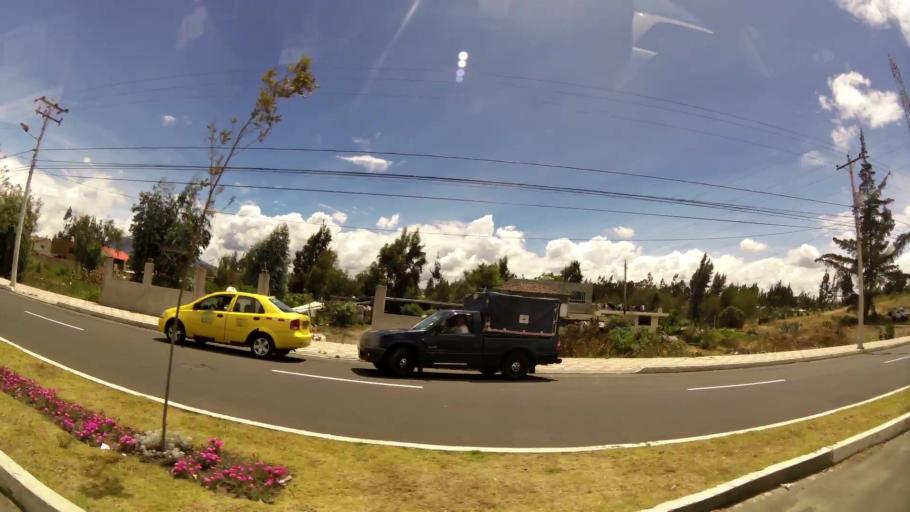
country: EC
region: Tungurahua
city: Ambato
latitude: -1.2697
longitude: -78.5936
